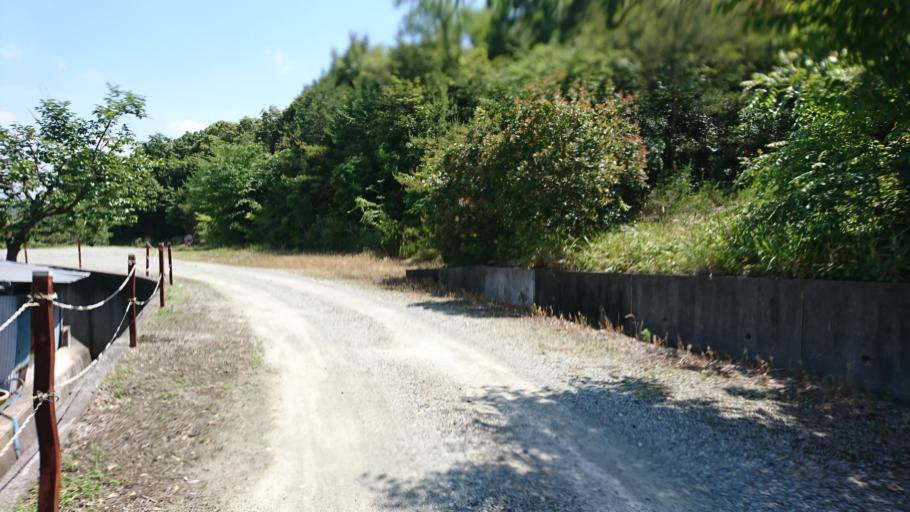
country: JP
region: Hyogo
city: Kakogawacho-honmachi
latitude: 34.8094
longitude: 134.7844
